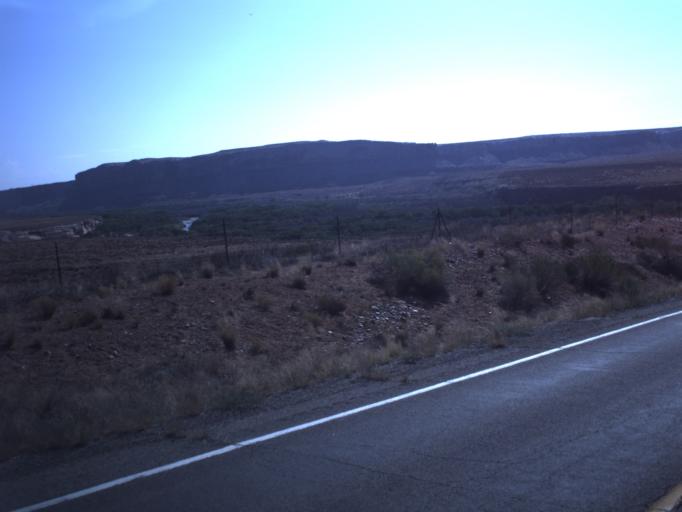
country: US
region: Utah
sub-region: San Juan County
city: Blanding
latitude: 37.2622
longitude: -109.6237
